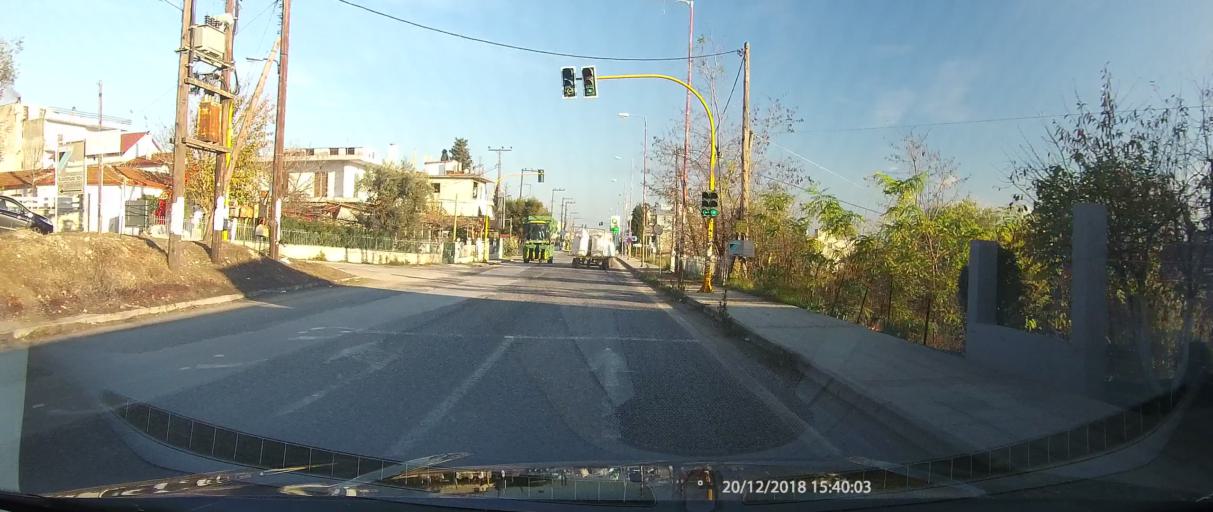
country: GR
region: Central Greece
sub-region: Nomos Fthiotidos
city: Stavros
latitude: 38.8935
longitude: 22.3723
